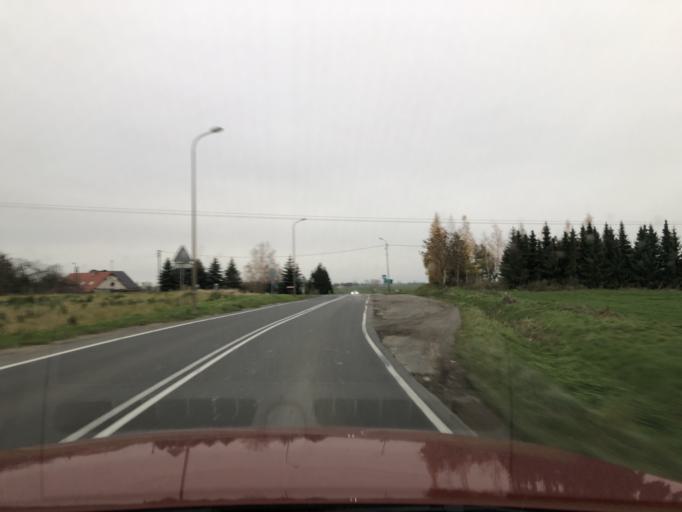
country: PL
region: Lower Silesian Voivodeship
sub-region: Powiat swidnicki
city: Zarow
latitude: 50.9838
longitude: 16.4902
